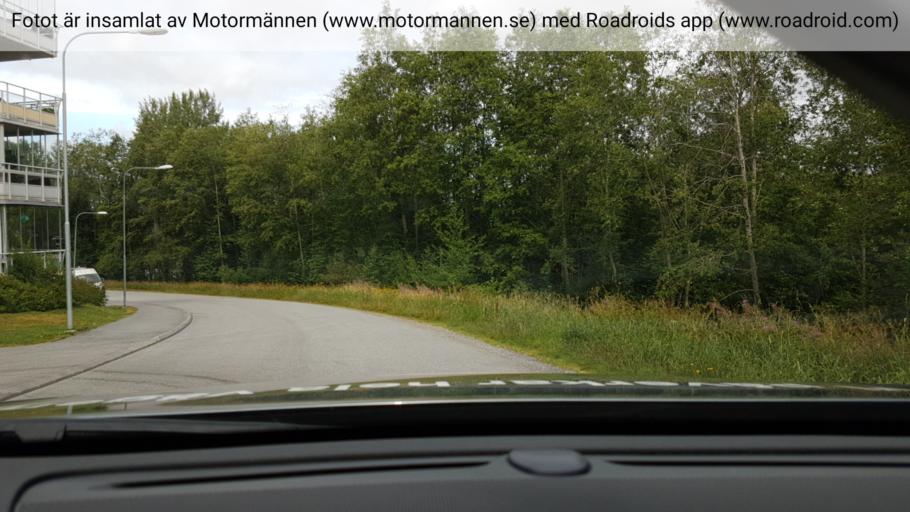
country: SE
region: Vaesterbotten
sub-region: Umea Kommun
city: Umea
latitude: 63.8237
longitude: 20.2315
